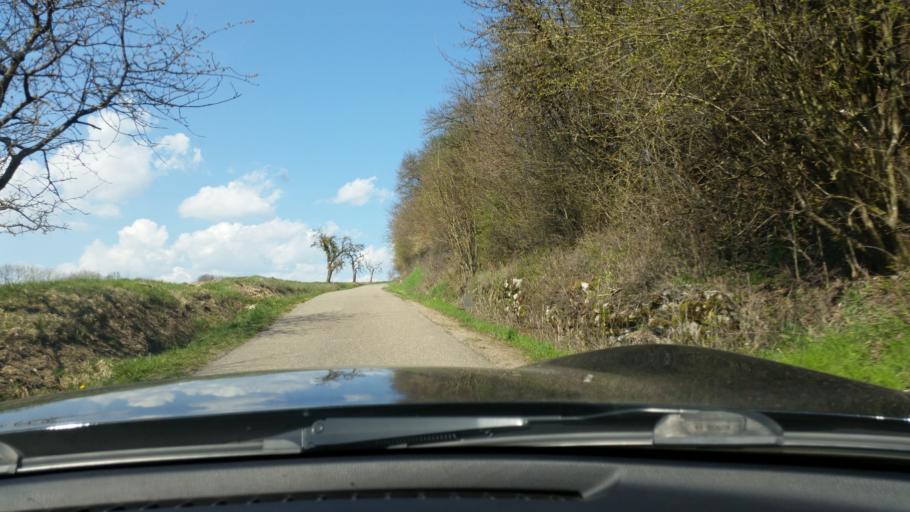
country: DE
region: Baden-Wuerttemberg
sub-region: Regierungsbezirk Stuttgart
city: Krautheim
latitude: 49.3726
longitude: 9.6127
